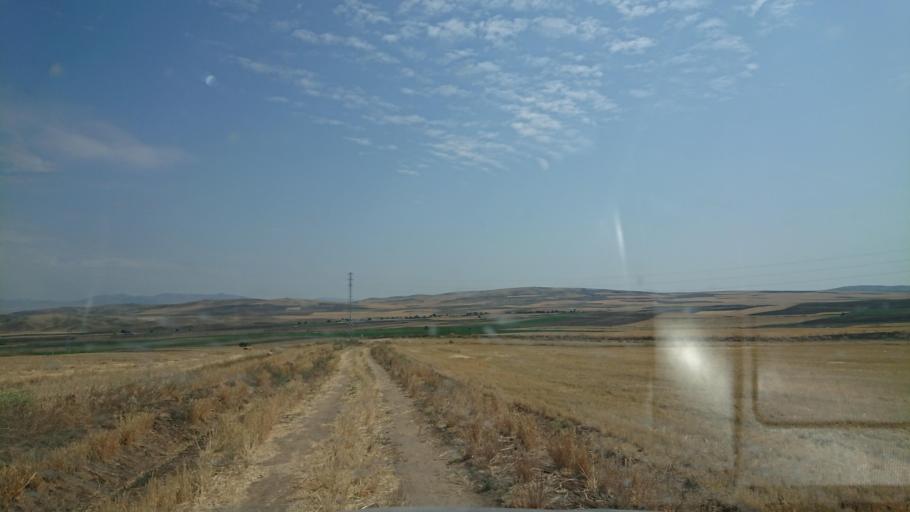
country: TR
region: Aksaray
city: Sariyahsi
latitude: 38.9538
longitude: 33.9114
